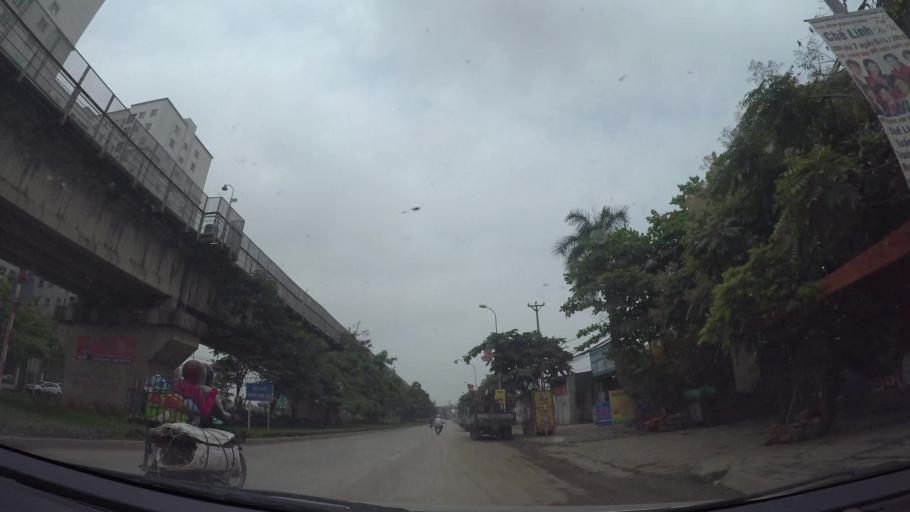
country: VN
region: Ha Noi
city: Tay Ho
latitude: 21.0828
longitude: 105.7858
